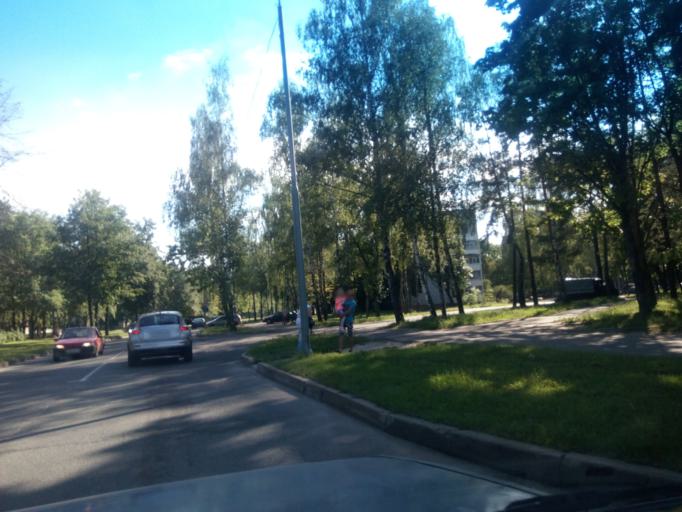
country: BY
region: Vitebsk
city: Navapolatsk
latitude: 55.5257
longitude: 28.6685
